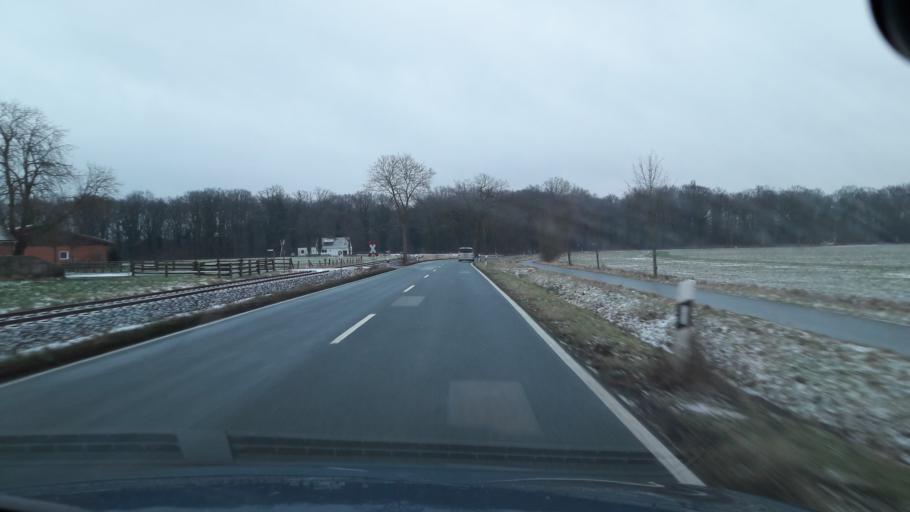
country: DE
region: North Rhine-Westphalia
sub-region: Regierungsbezirk Arnsberg
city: Lippstadt
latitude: 51.6889
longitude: 8.2898
